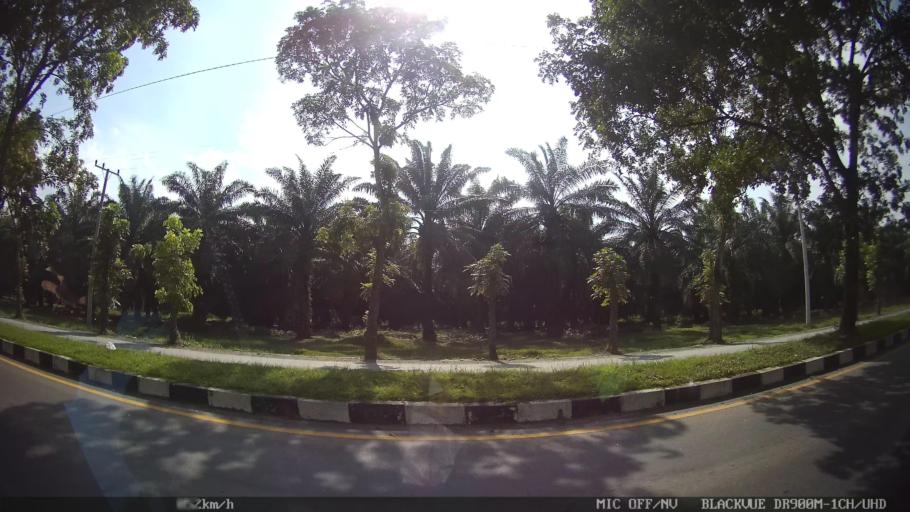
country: ID
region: North Sumatra
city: Binjai
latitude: 3.6385
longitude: 98.5353
